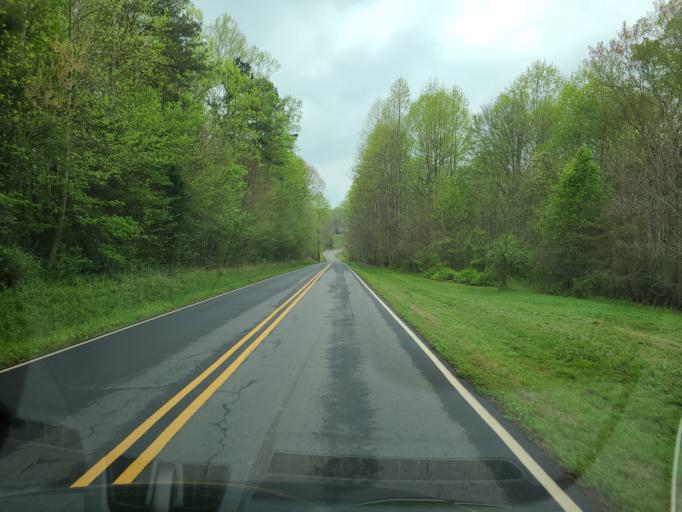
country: US
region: North Carolina
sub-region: Lincoln County
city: Lincolnton
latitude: 35.4593
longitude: -81.3330
